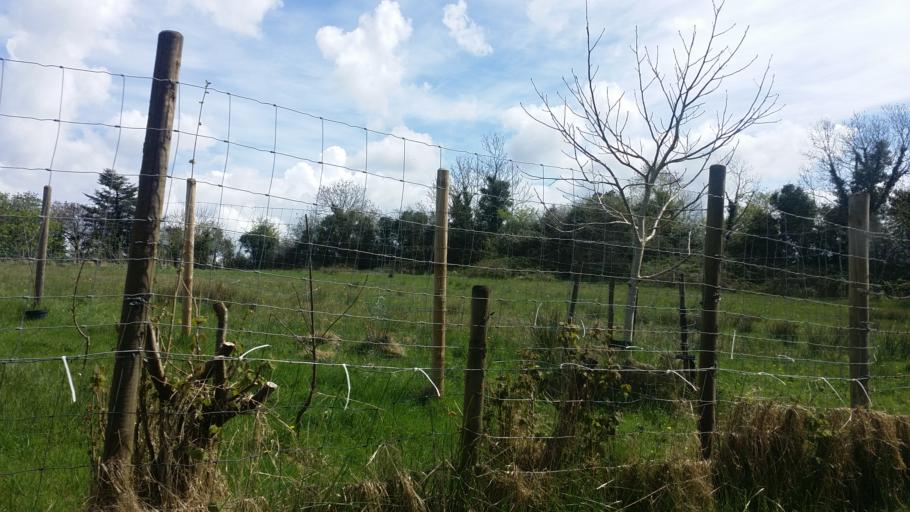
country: GB
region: Northern Ireland
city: Lisnaskea
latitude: 54.1885
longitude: -7.4910
